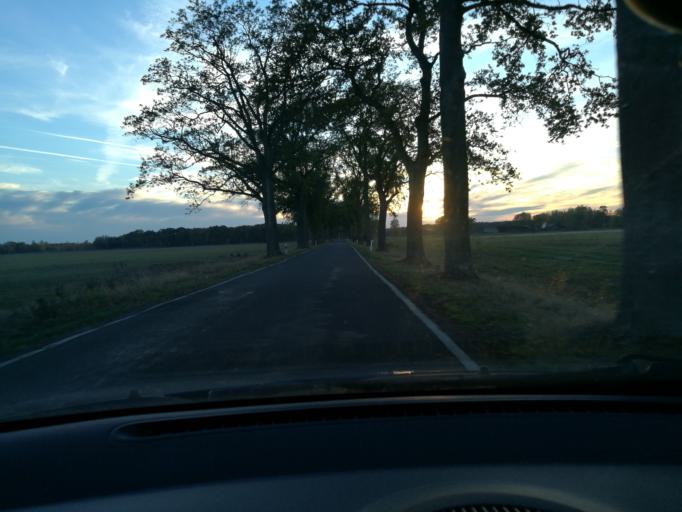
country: DE
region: Brandenburg
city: Cumlosen
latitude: 53.0924
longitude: 11.6699
